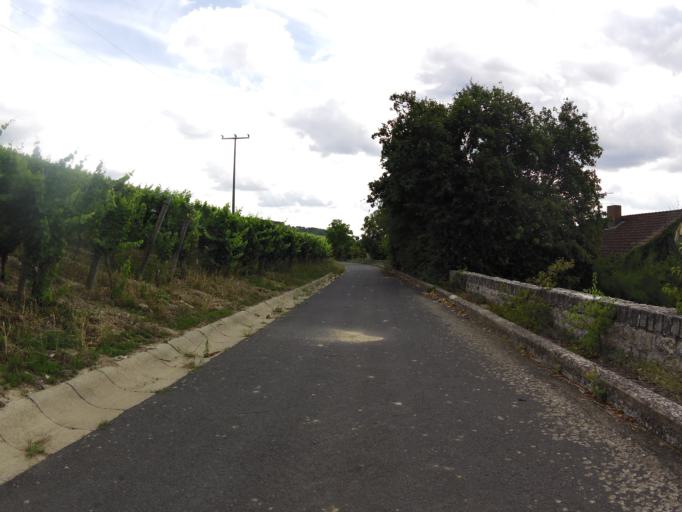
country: DE
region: Bavaria
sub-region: Regierungsbezirk Unterfranken
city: Sommerhausen
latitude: 49.7032
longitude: 10.0295
